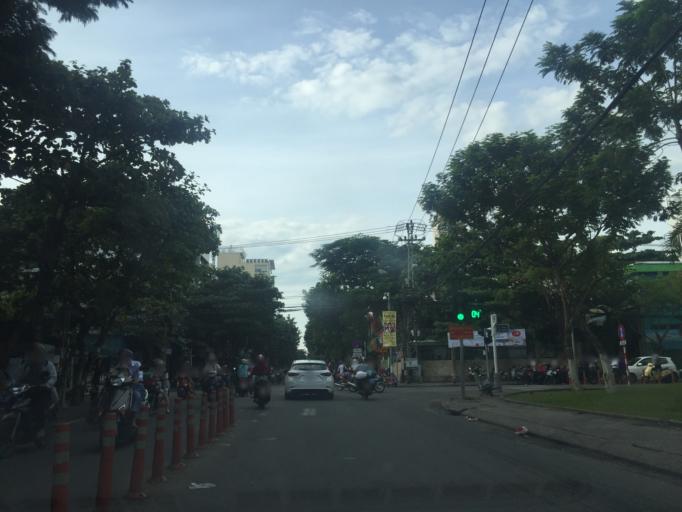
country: VN
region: Da Nang
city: Da Nang
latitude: 16.0720
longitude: 108.2131
